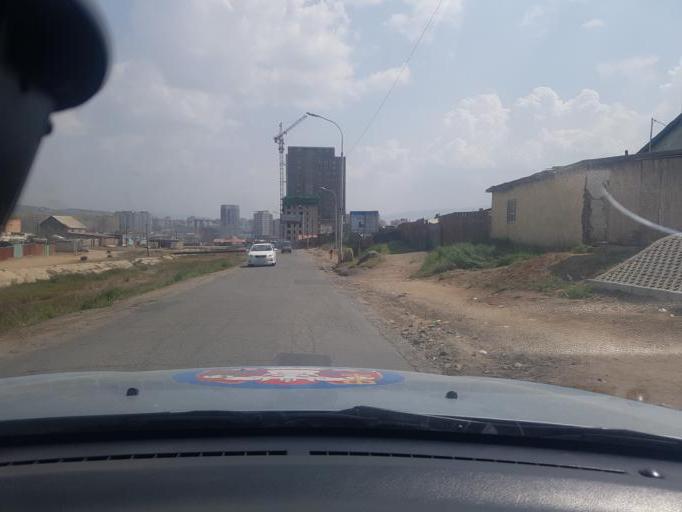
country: MN
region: Ulaanbaatar
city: Ulaanbaatar
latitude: 47.9359
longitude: 106.9031
